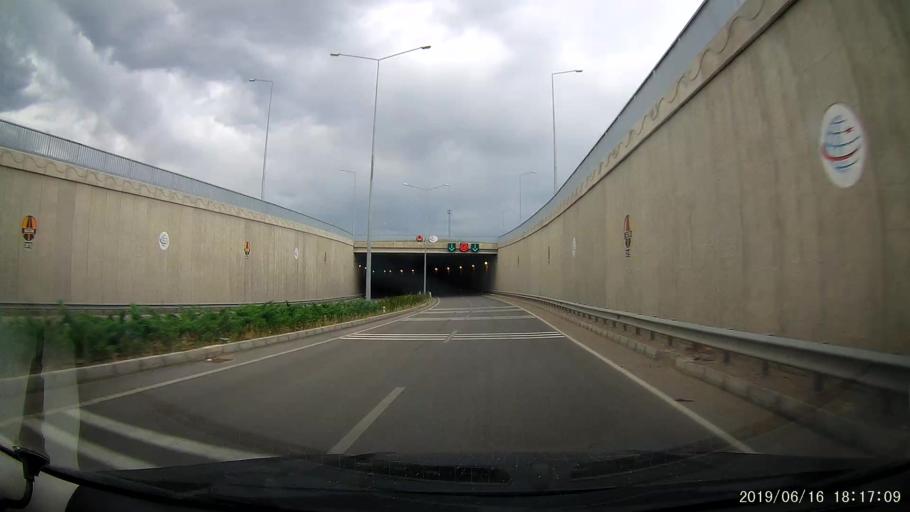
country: TR
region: Erzincan
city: Erzincan
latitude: 39.7327
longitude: 39.5372
